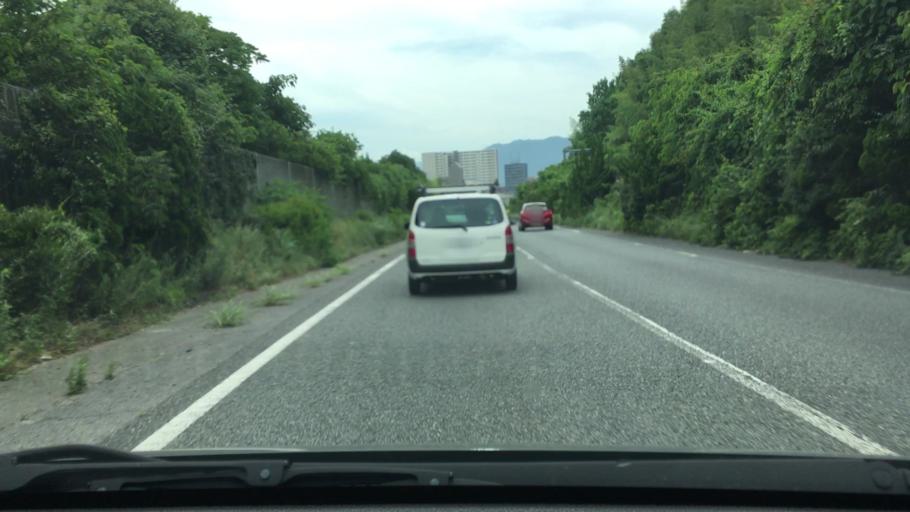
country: JP
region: Hiroshima
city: Hatsukaichi
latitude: 34.3790
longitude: 132.3886
